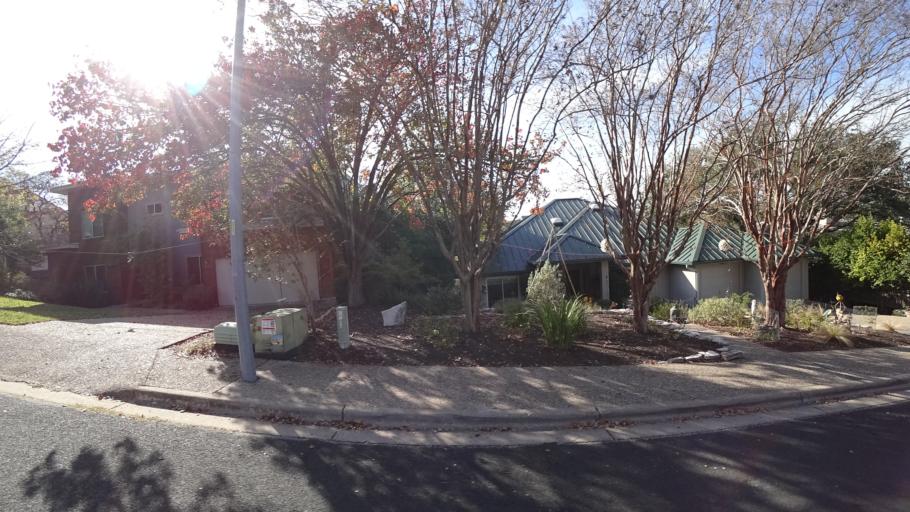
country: US
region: Texas
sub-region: Williamson County
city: Jollyville
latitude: 30.3805
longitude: -97.7579
